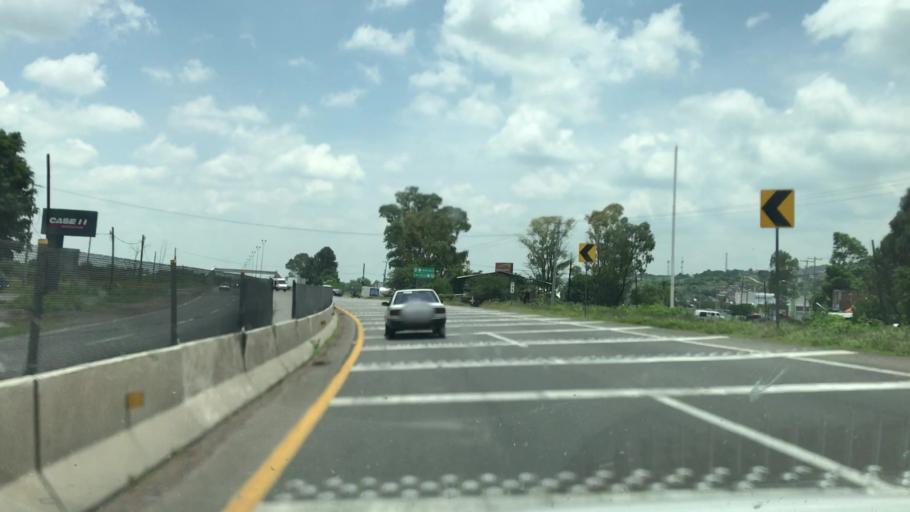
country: MX
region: Guanajuato
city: Abasolo
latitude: 20.4505
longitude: -101.5516
